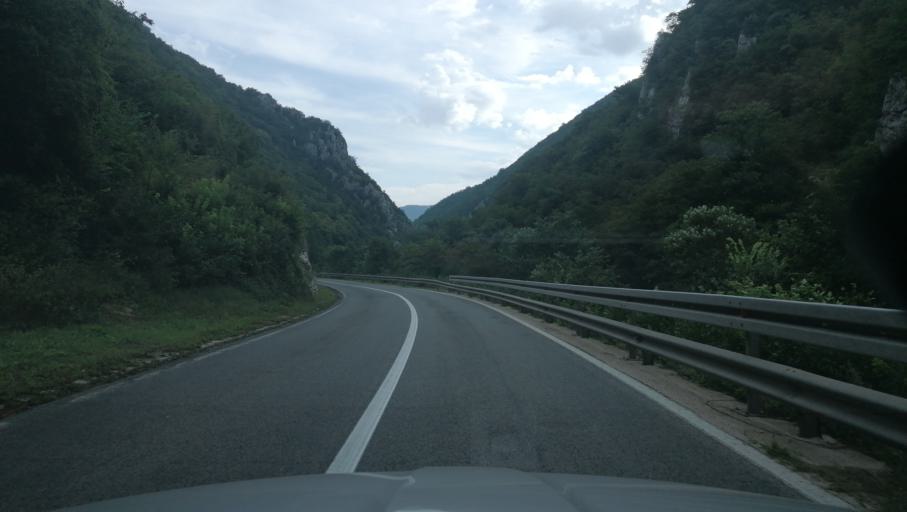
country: BA
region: Republika Srpska
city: Hiseti
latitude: 44.6004
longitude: 17.1313
